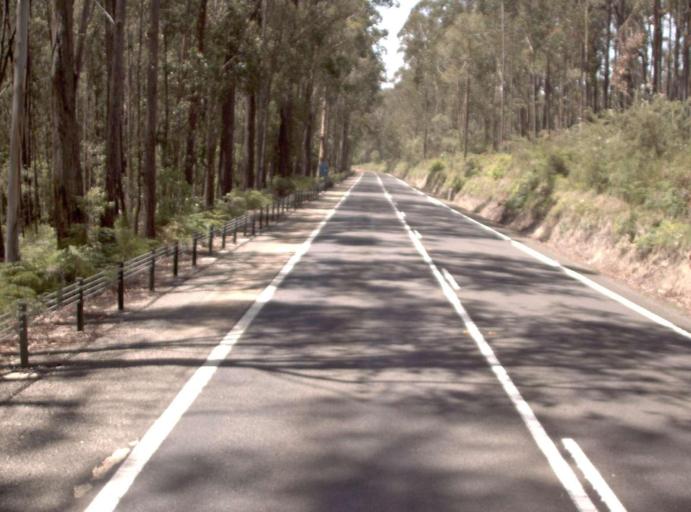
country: AU
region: New South Wales
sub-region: Bombala
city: Bombala
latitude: -37.6562
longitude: 148.8119
